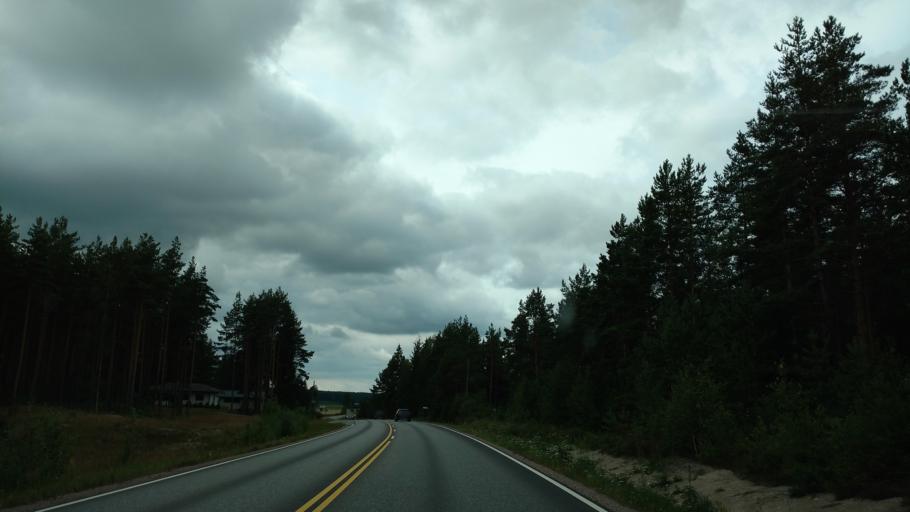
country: FI
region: Varsinais-Suomi
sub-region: Aboland-Turunmaa
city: Vaestanfjaerd
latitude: 60.1138
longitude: 22.6099
